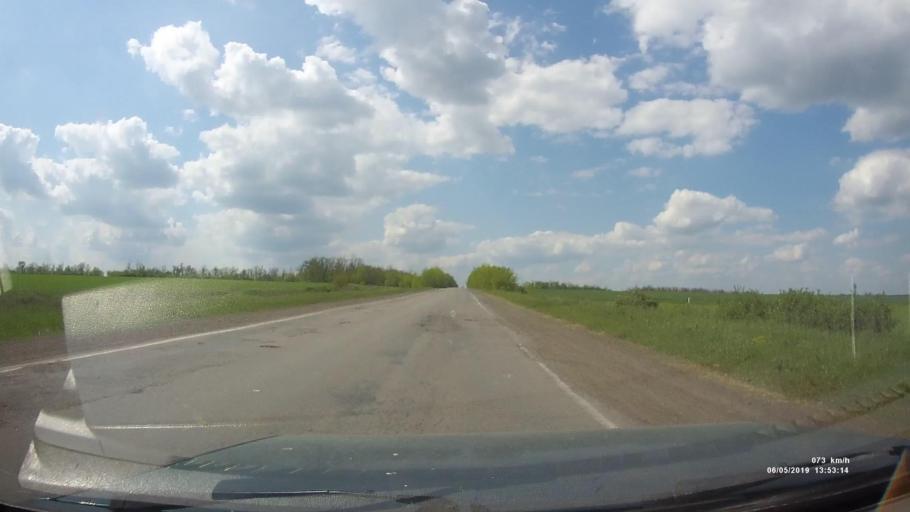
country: RU
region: Rostov
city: Melikhovskaya
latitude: 47.6671
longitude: 40.4653
